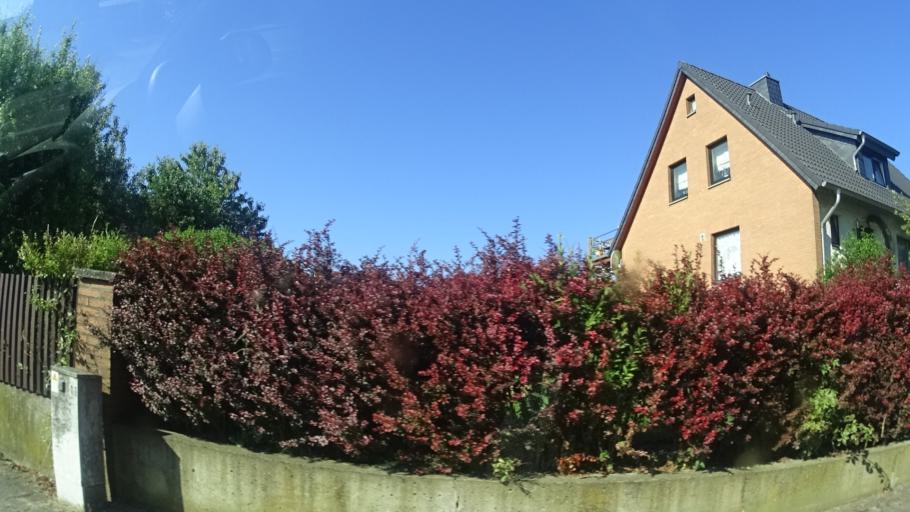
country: DE
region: Lower Saxony
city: Bad Salzdetfurth
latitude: 52.1047
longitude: 10.0325
